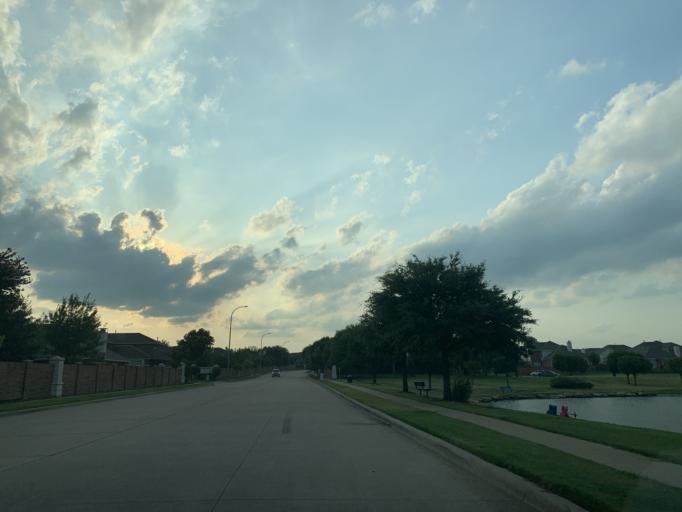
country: US
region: Texas
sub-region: Tarrant County
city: Keller
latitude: 32.9424
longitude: -97.2718
